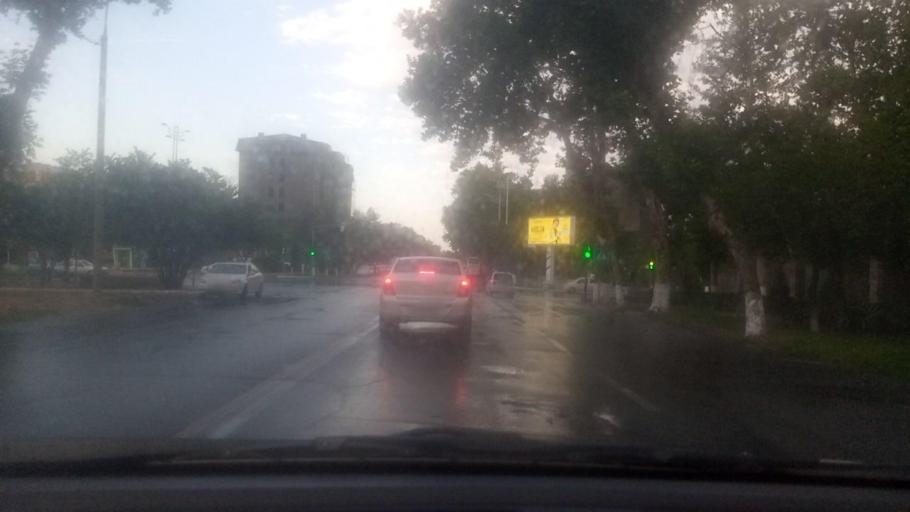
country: UZ
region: Toshkent Shahri
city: Tashkent
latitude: 41.2957
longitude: 69.1770
